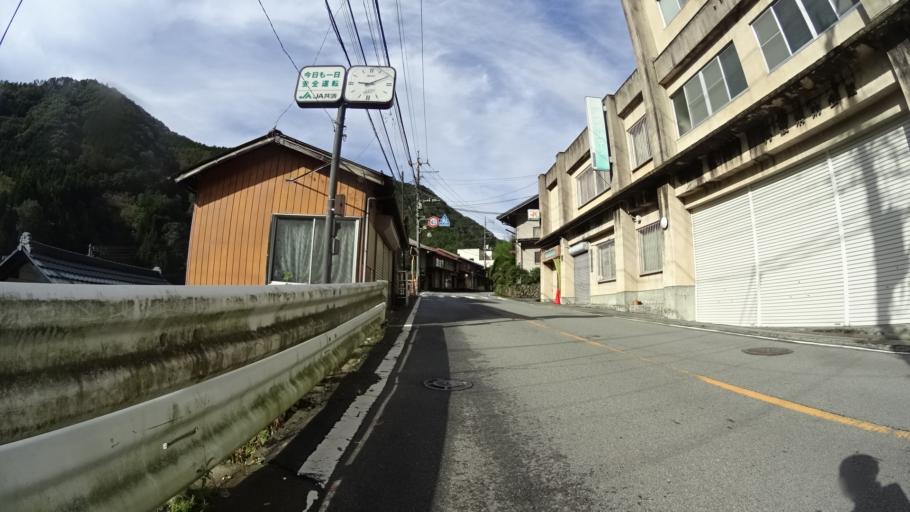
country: JP
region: Yamanashi
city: Otsuki
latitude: 35.7908
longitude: 138.9211
